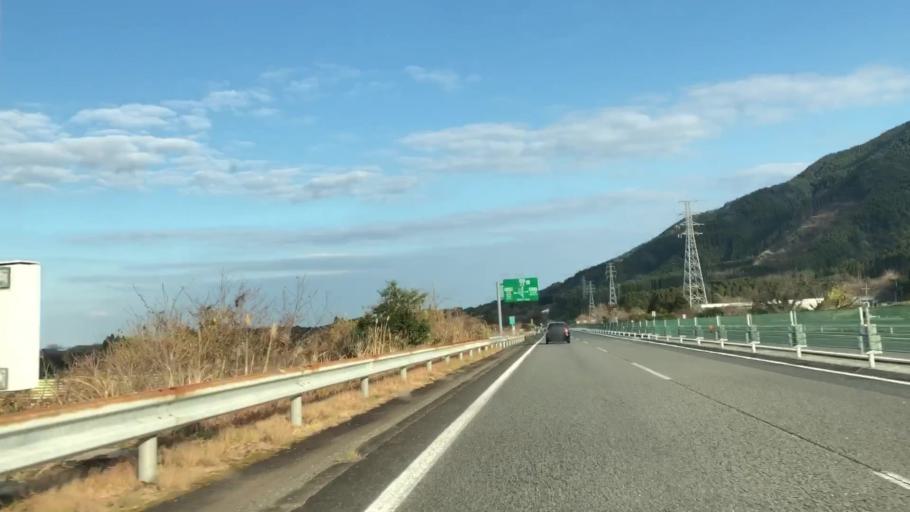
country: JP
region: Miyazaki
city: Miyazaki-shi
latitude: 31.8328
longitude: 131.3282
